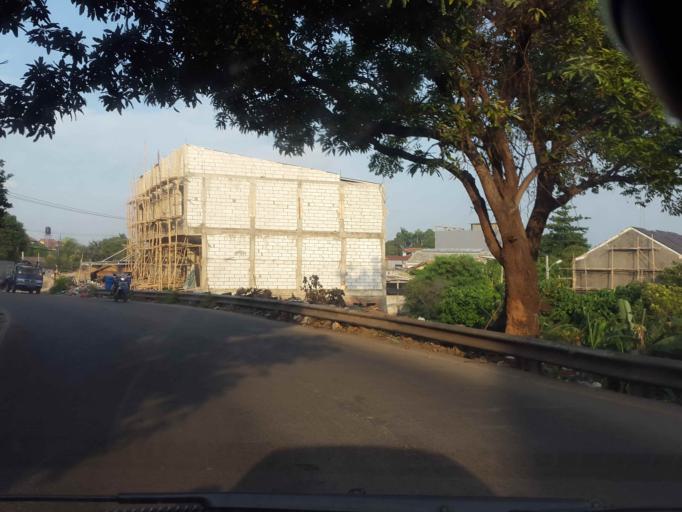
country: ID
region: Banten
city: South Tangerang
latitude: -6.2626
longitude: 106.7191
